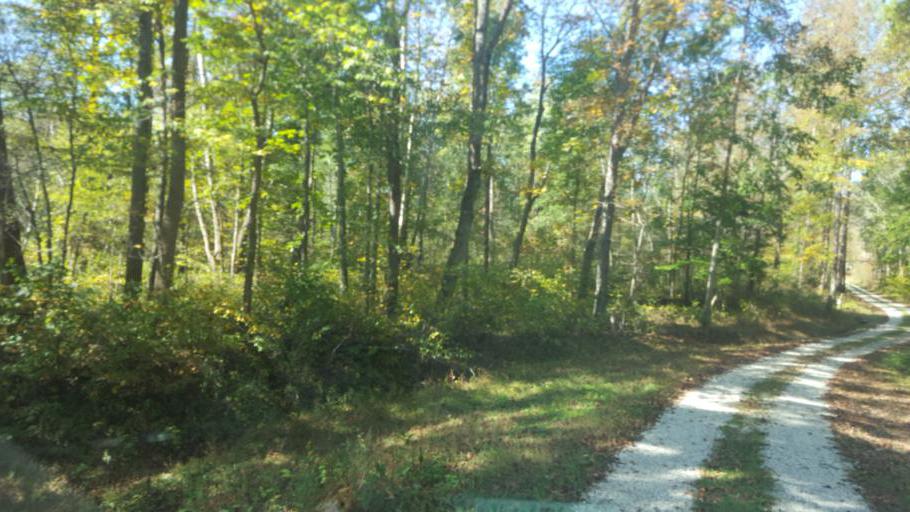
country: US
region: Kentucky
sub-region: Fleming County
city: Flemingsburg
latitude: 38.4603
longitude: -83.5706
